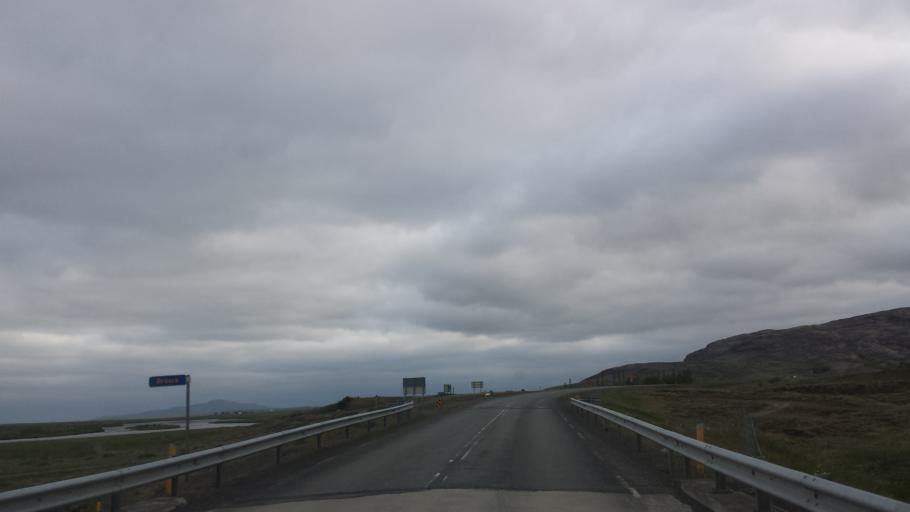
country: IS
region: South
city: Selfoss
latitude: 64.1450
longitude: -20.5570
